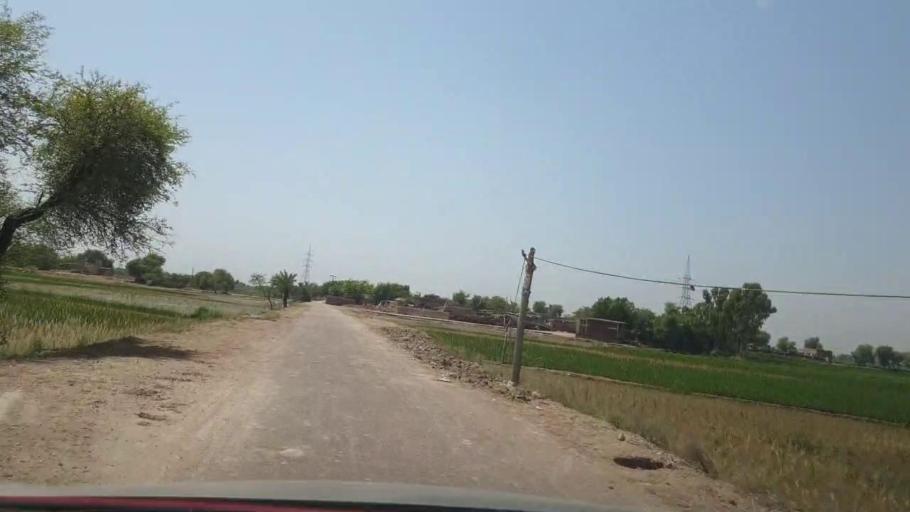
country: PK
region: Sindh
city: Warah
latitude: 27.4967
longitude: 67.7502
